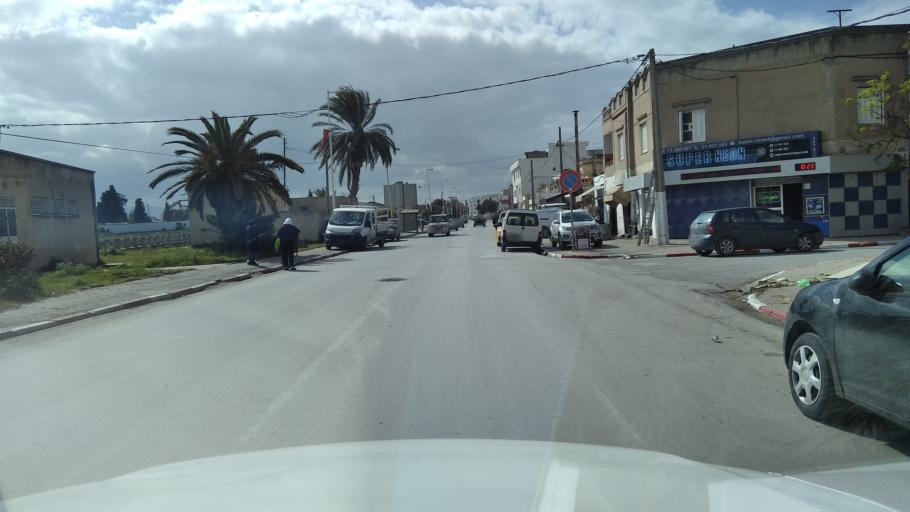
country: TN
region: Bin 'Arus
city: Ben Arous
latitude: 36.7475
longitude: 10.2257
